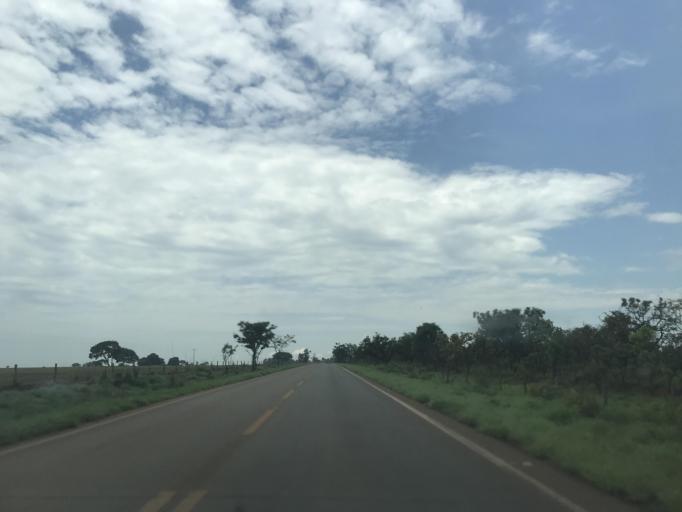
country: BR
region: Goias
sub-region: Luziania
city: Luziania
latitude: -16.2884
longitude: -48.0034
